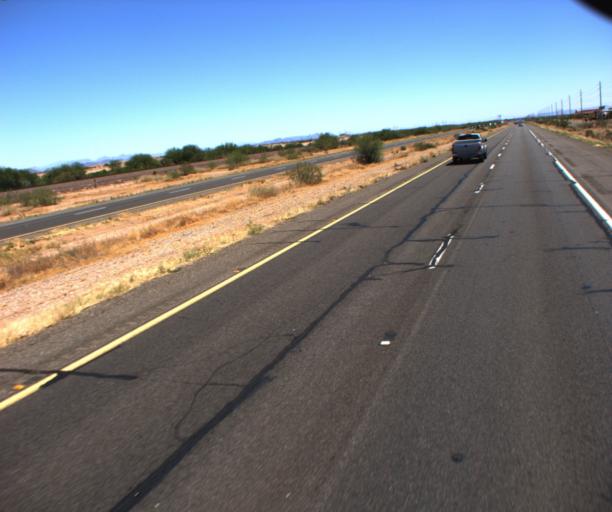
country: US
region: Arizona
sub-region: Maricopa County
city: Sun City West
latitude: 33.7102
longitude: -112.4421
